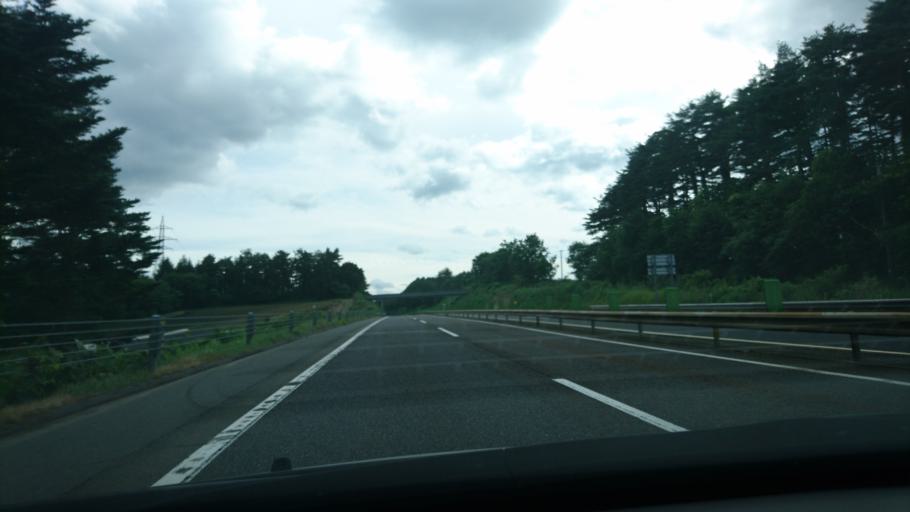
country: JP
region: Aomori
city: Hachinohe
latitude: 40.4336
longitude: 141.4446
